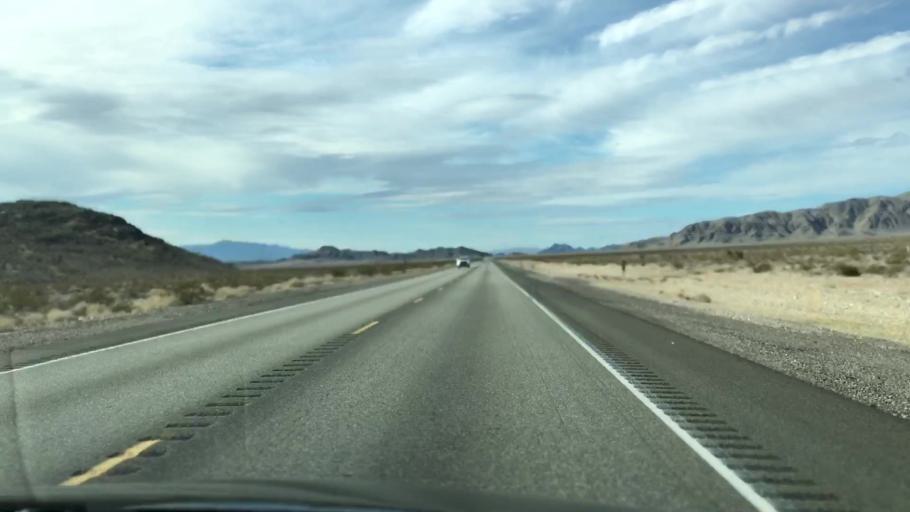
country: US
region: Nevada
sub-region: Nye County
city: Pahrump
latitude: 36.5673
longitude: -116.1423
